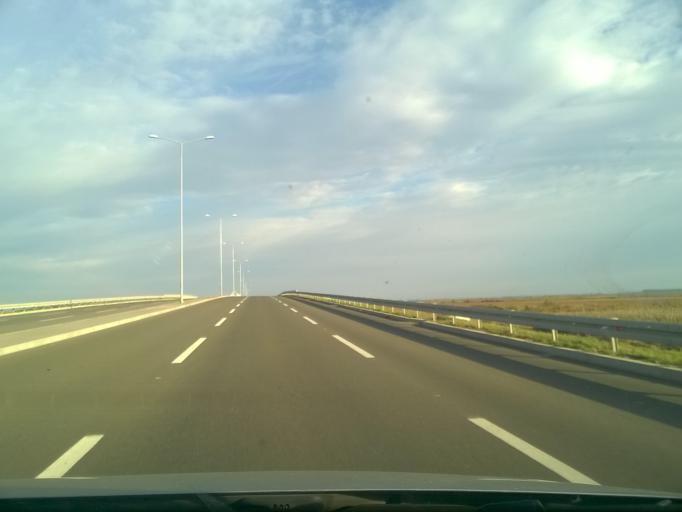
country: RS
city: Ovca
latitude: 44.9062
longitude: 20.5125
